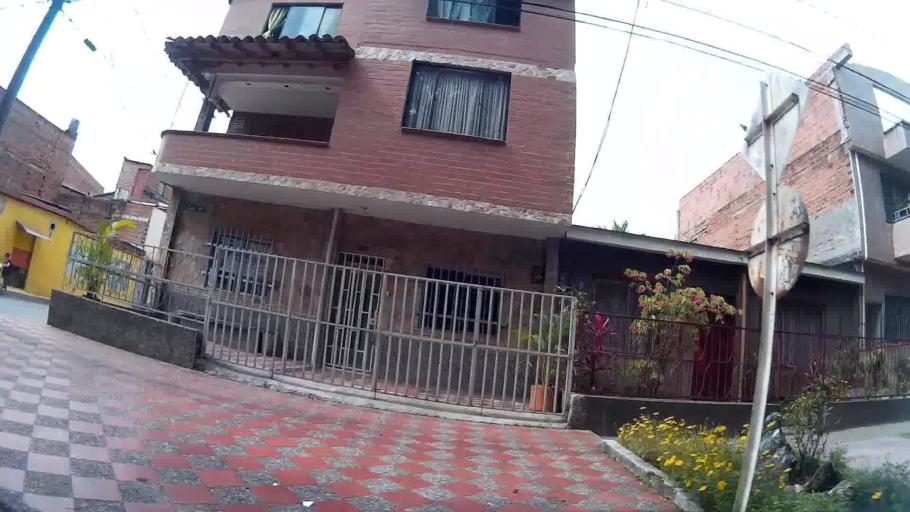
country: CO
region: Antioquia
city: Medellin
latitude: 6.2587
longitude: -75.6062
